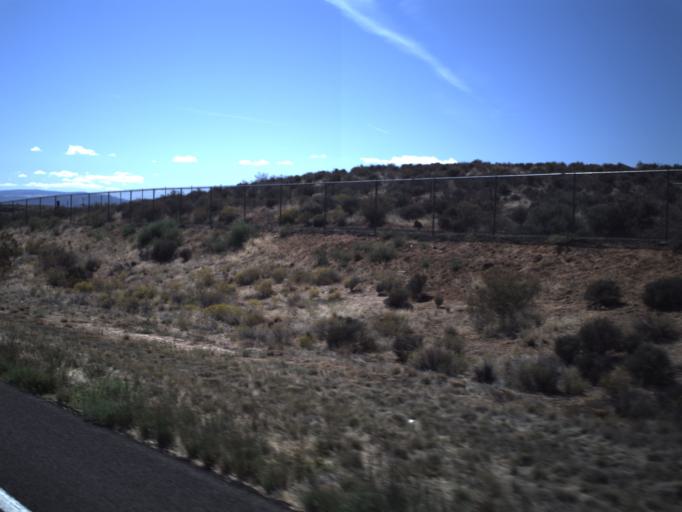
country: US
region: Utah
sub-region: Washington County
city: Ivins
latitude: 37.2036
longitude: -113.6268
